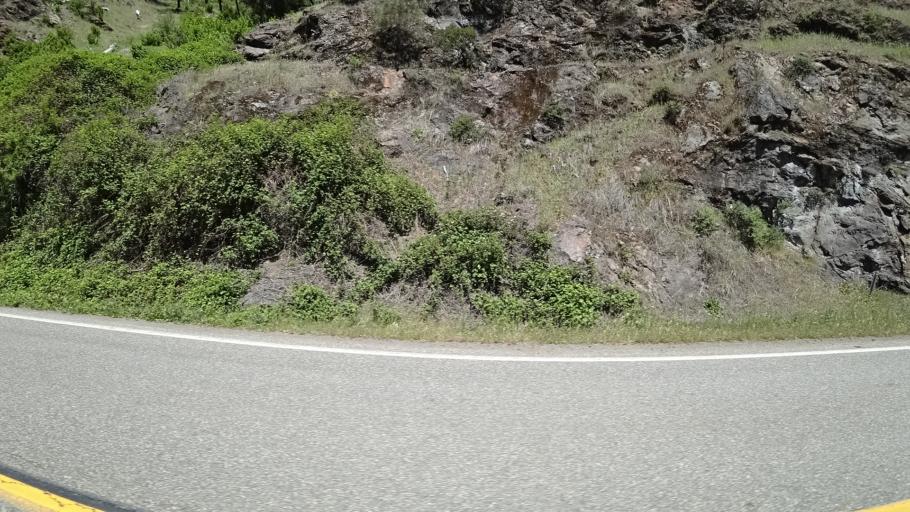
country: US
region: California
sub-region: Trinity County
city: Hayfork
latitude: 40.7616
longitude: -123.2828
